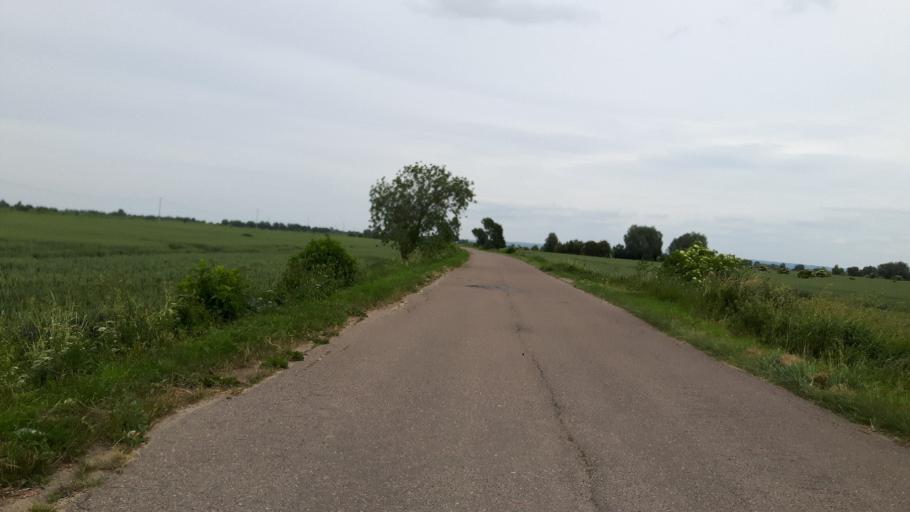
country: PL
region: Pomeranian Voivodeship
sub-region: Powiat nowodworski
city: Sztutowo
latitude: 54.2689
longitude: 19.1873
